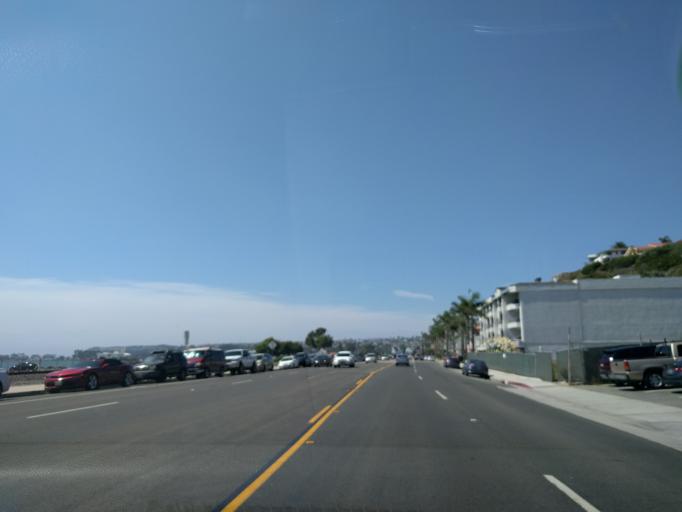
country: US
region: California
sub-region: Orange County
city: Dana Point
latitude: 33.4589
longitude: -117.6732
